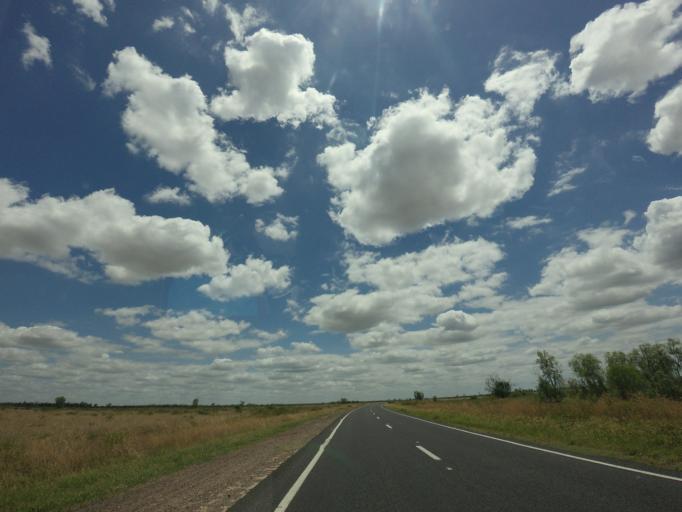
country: AU
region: New South Wales
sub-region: Moree Plains
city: Boggabilla
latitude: -28.7065
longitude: 150.2801
